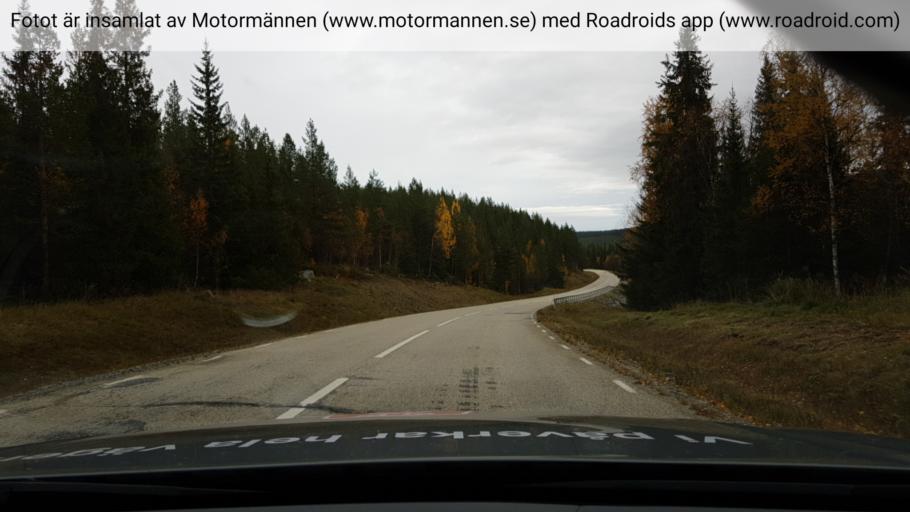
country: SE
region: Jaemtland
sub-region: Are Kommun
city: Are
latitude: 62.8141
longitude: 12.9389
